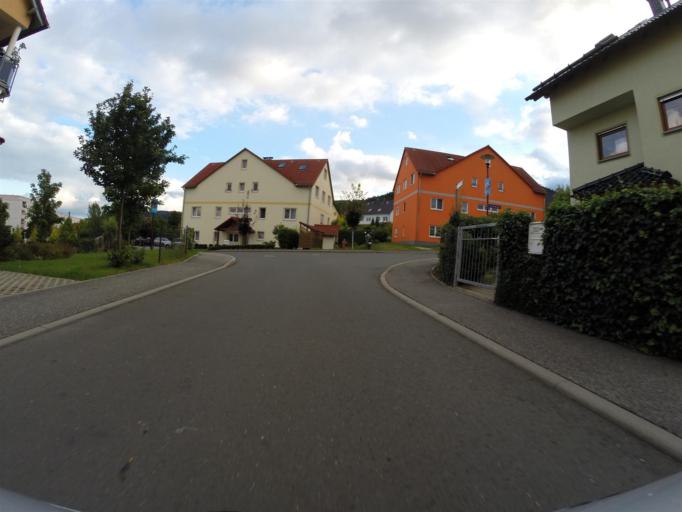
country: DE
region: Thuringia
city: Jena
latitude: 50.9011
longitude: 11.5689
